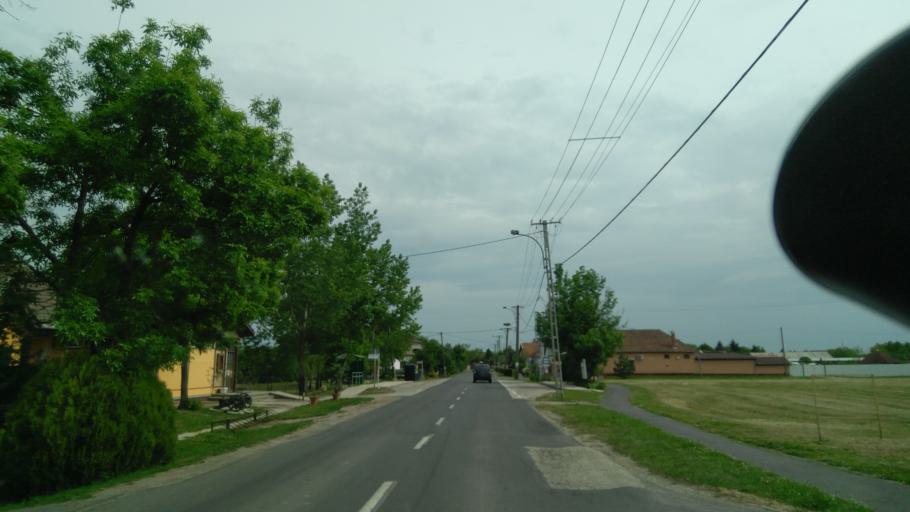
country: HU
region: Bekes
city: Sarkad
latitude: 46.8031
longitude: 21.3838
